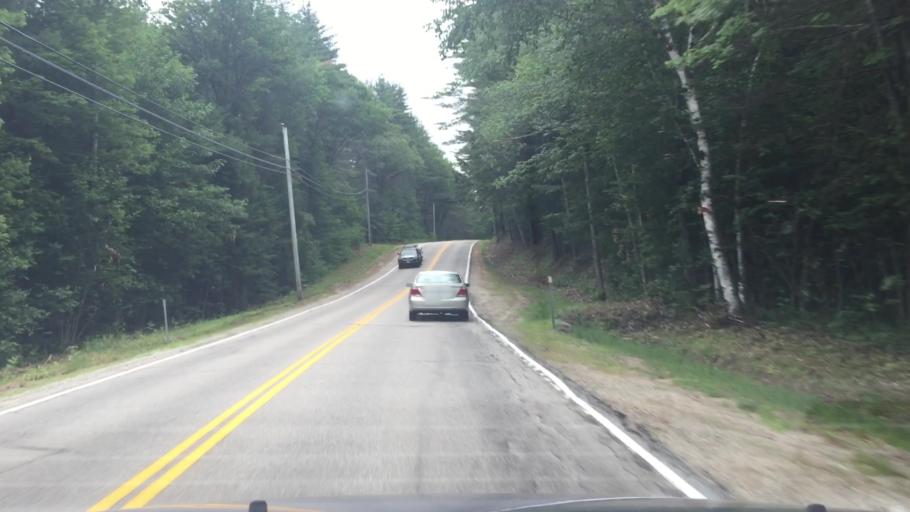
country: US
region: New Hampshire
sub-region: Carroll County
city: Conway
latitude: 43.9256
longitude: -71.0794
